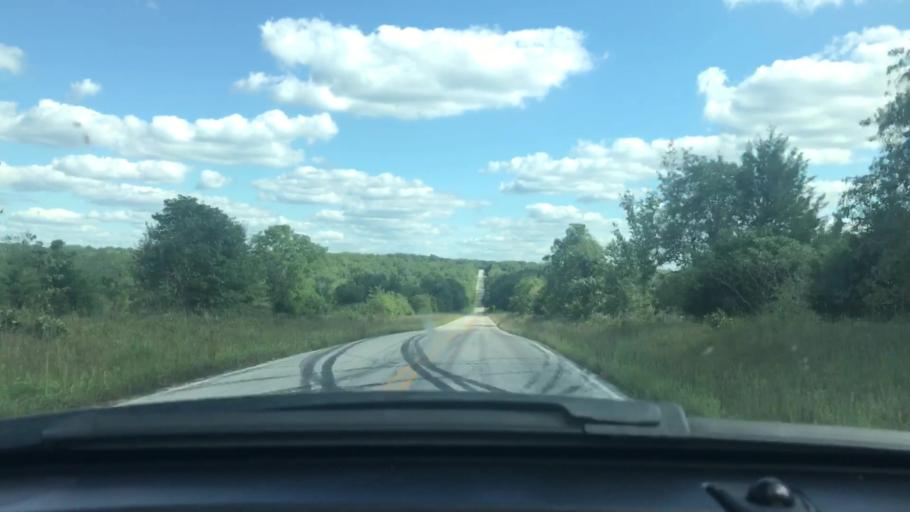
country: US
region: Missouri
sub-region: Wright County
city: Hartville
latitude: 37.3878
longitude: -92.4453
